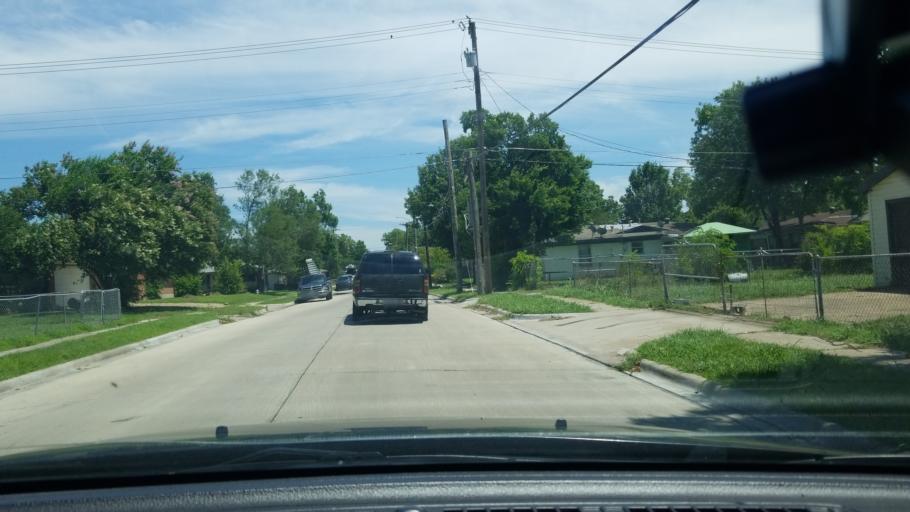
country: US
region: Texas
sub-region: Dallas County
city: Mesquite
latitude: 32.7875
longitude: -96.6173
